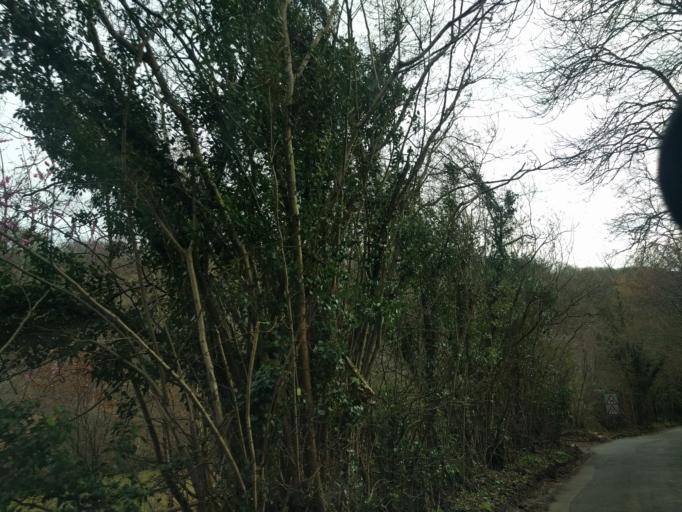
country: GB
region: England
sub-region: Wiltshire
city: Colerne
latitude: 51.4598
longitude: -2.2836
